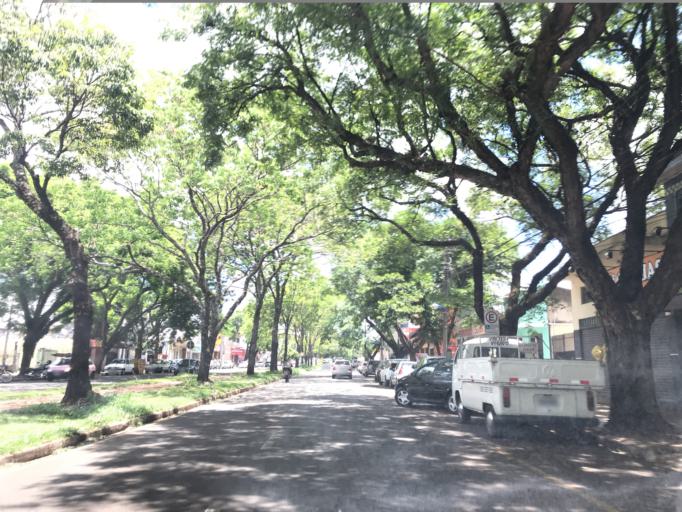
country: BR
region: Parana
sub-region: Maringa
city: Maringa
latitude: -23.3974
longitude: -51.9190
